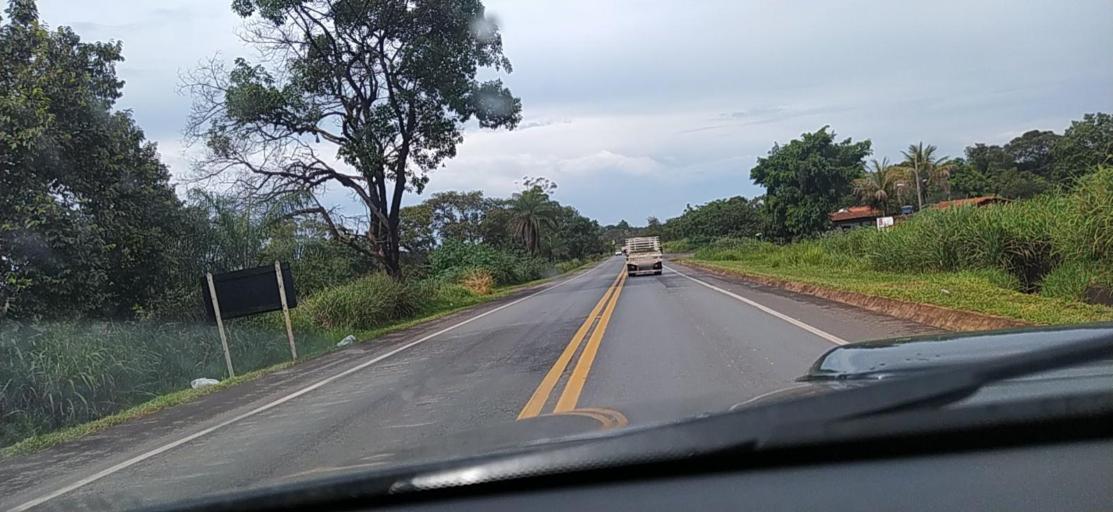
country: BR
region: Minas Gerais
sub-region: Montes Claros
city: Montes Claros
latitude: -16.8755
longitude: -43.8595
